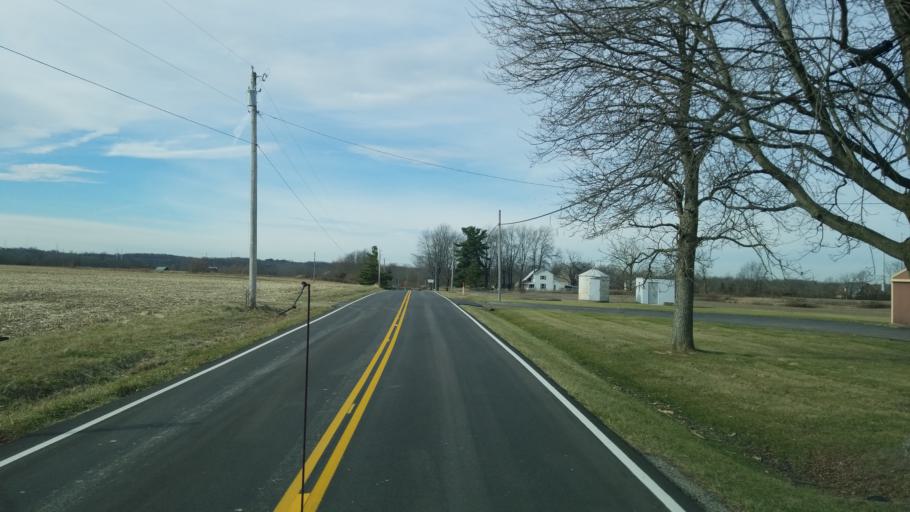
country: US
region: Ohio
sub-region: Warren County
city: Morrow
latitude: 39.4296
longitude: -84.0923
